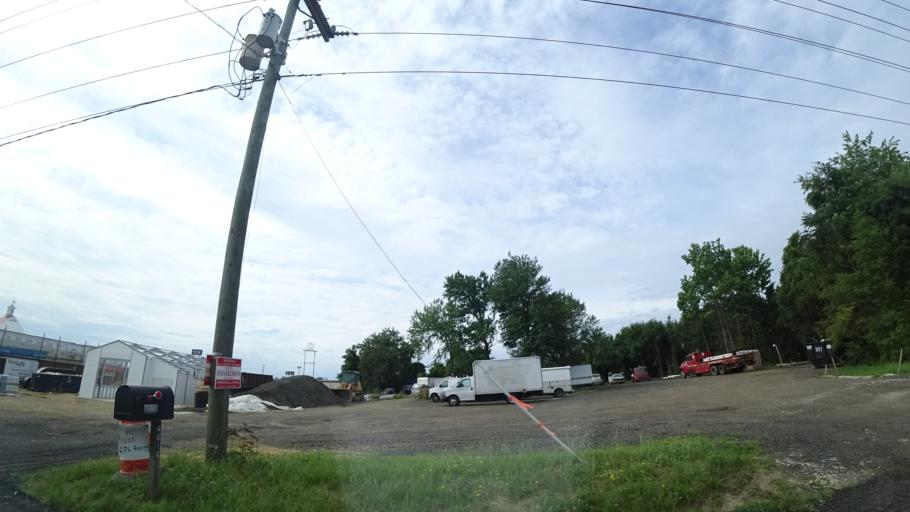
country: US
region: Virginia
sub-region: City of Fredericksburg
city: Fredericksburg
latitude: 38.2496
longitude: -77.5006
